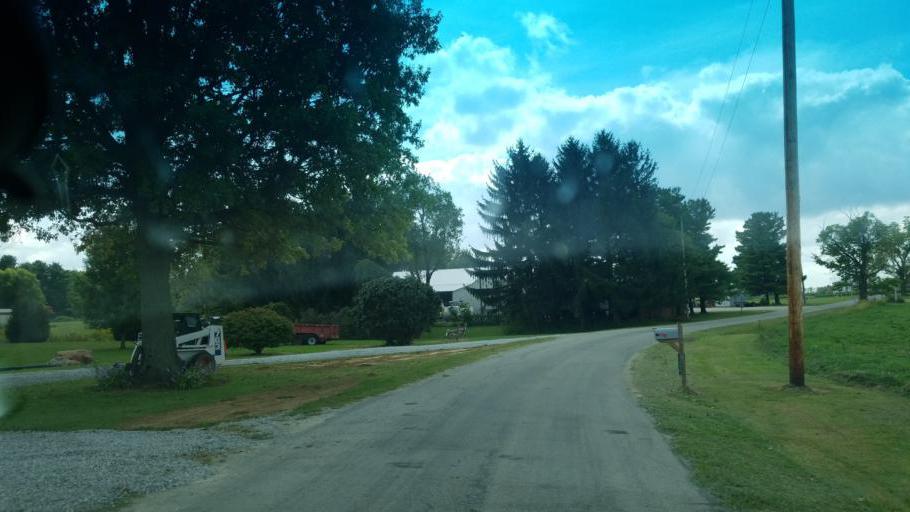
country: US
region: Ohio
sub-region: Seneca County
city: Tiffin
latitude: 40.9520
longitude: -83.1520
